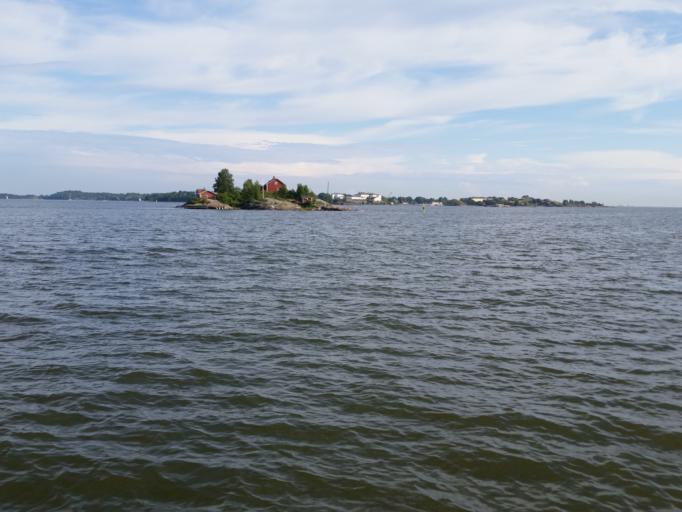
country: FI
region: Uusimaa
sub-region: Helsinki
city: Helsinki
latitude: 60.1619
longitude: 24.9692
